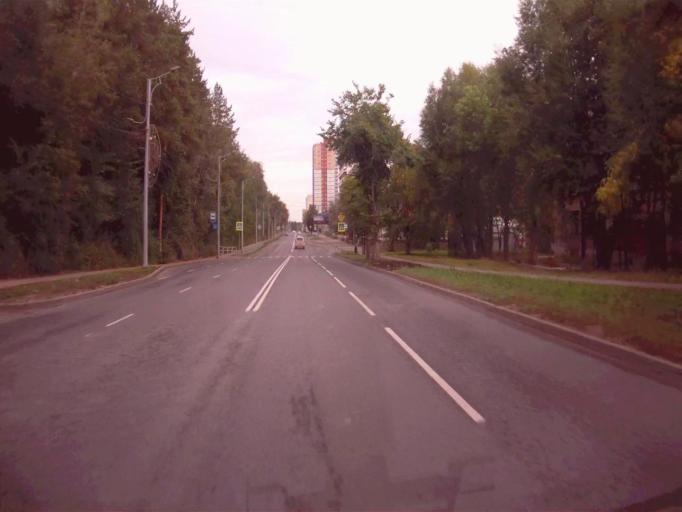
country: RU
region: Chelyabinsk
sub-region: Gorod Chelyabinsk
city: Chelyabinsk
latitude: 55.1518
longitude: 61.3651
